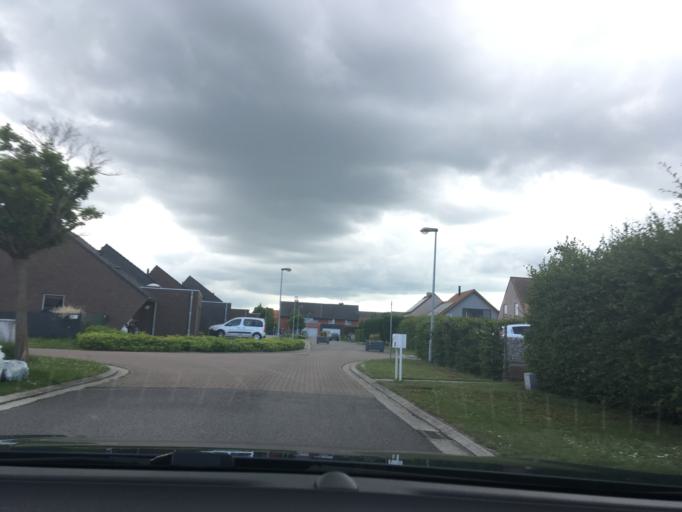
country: BE
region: Flanders
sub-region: Provincie West-Vlaanderen
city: Moorslede
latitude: 50.9378
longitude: 3.0631
